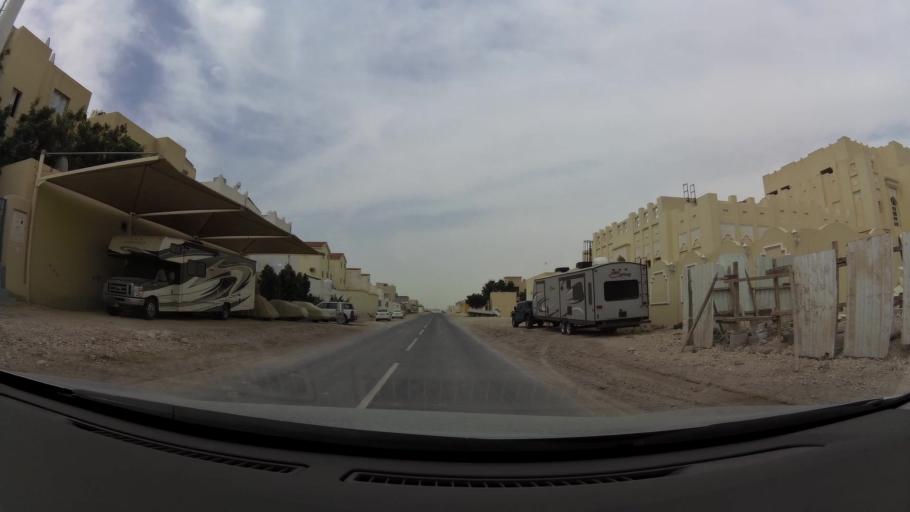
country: QA
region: Baladiyat ad Dawhah
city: Doha
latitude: 25.2162
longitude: 51.4755
